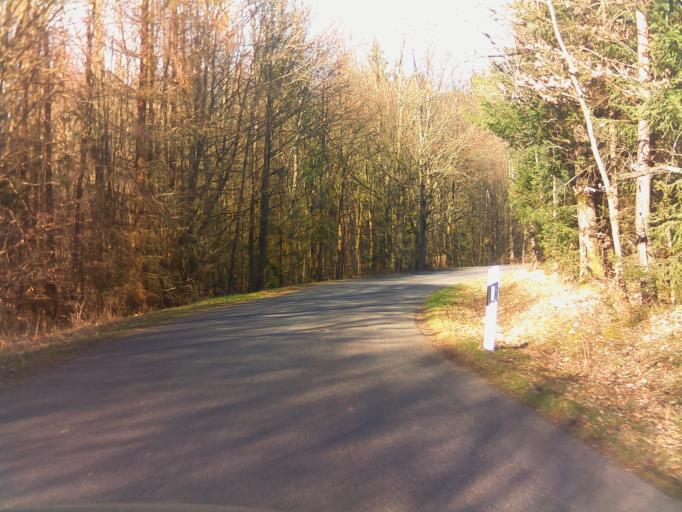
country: DE
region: Bavaria
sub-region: Regierungsbezirk Unterfranken
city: Willmars
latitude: 50.4969
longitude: 10.2939
